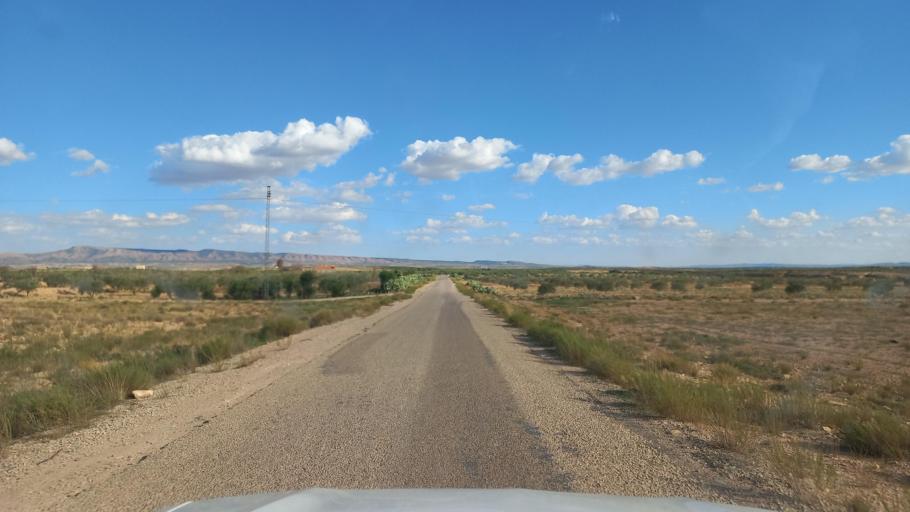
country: TN
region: Al Qasrayn
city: Sbiba
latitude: 35.3888
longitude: 9.0281
